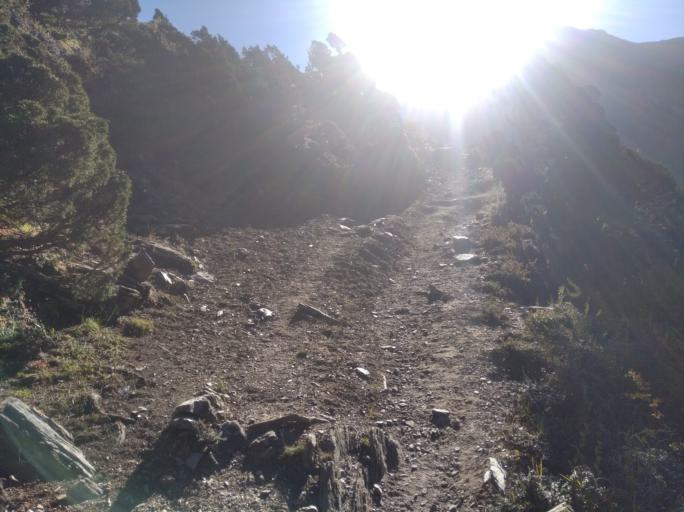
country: NP
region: Western Region
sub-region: Dhawalagiri Zone
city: Jomsom
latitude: 28.9005
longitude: 83.3631
